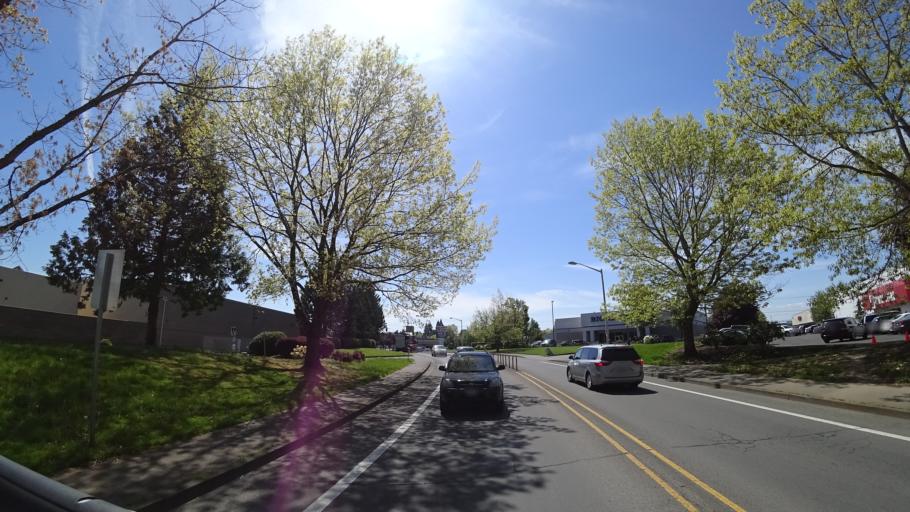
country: US
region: Oregon
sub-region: Washington County
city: Hillsboro
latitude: 45.5087
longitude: -122.9596
